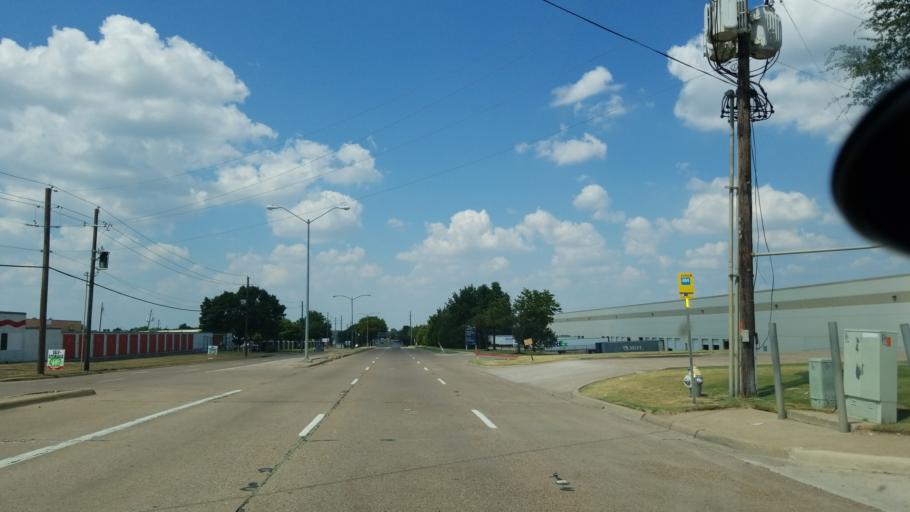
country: US
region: Texas
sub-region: Dallas County
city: Duncanville
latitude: 32.6800
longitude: -96.8827
